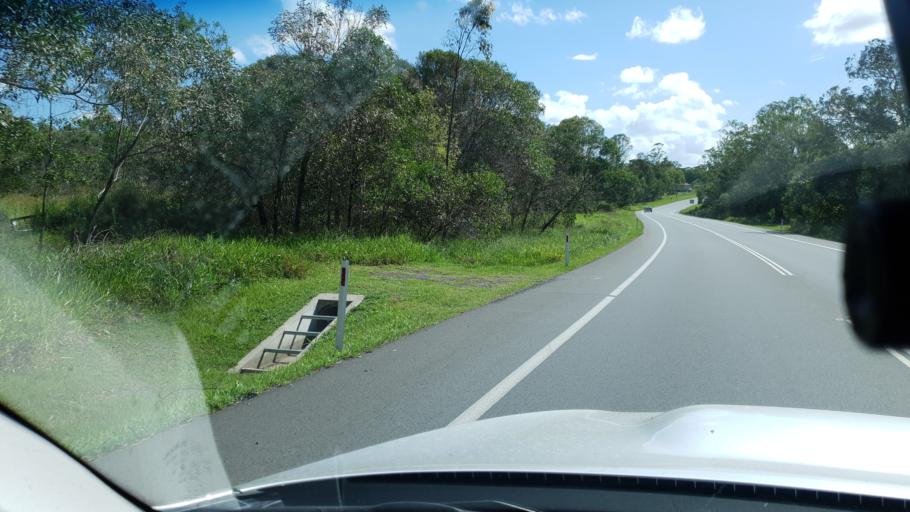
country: AU
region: Queensland
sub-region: Logan
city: Woodridge
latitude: -27.6482
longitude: 153.0866
